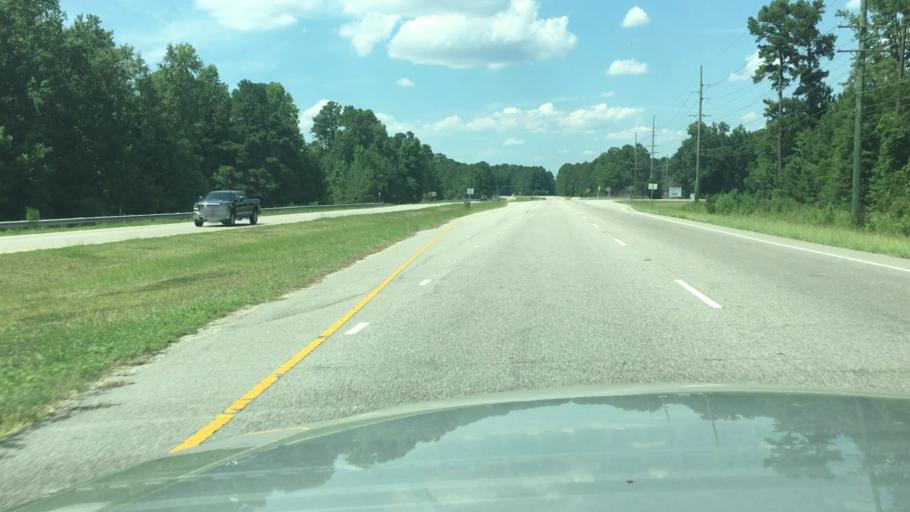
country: US
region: North Carolina
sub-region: Cumberland County
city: Vander
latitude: 34.9533
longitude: -78.8442
